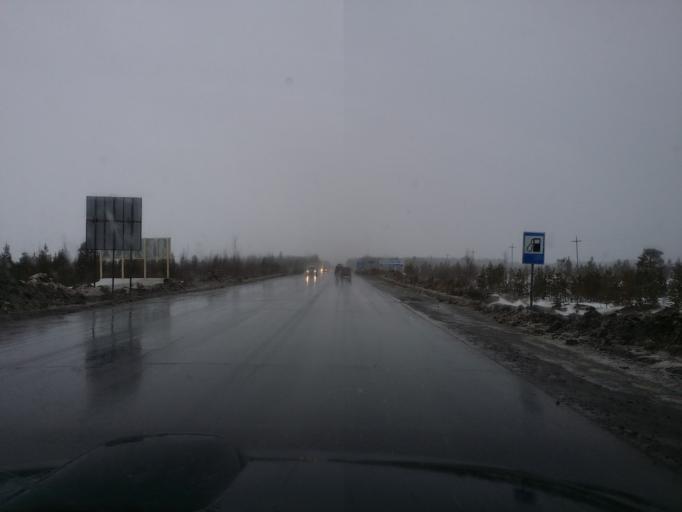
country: RU
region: Khanty-Mansiyskiy Avtonomnyy Okrug
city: Nizhnevartovsk
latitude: 60.9565
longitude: 76.7191
